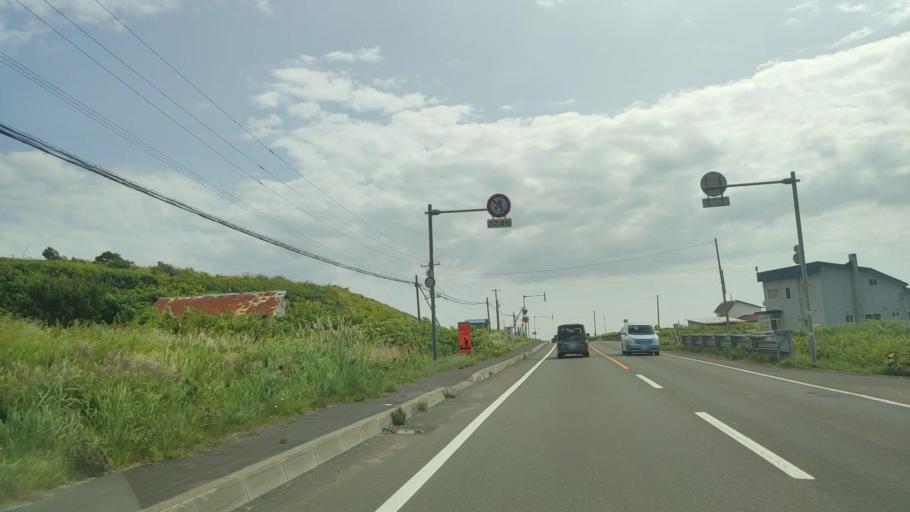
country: JP
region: Hokkaido
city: Rumoi
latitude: 44.2572
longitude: 141.6568
